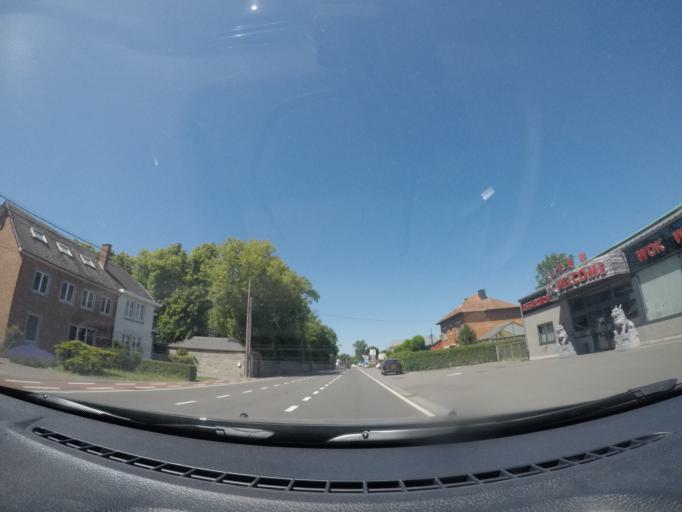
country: BE
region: Wallonia
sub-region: Province de Namur
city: Beauraing
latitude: 50.1167
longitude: 4.9553
